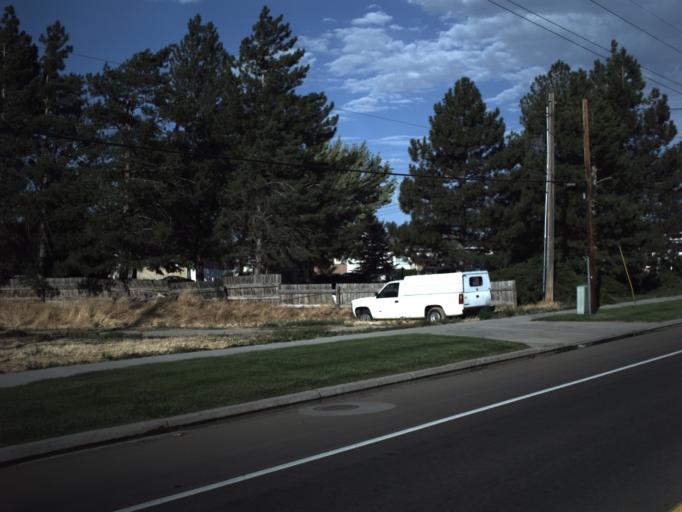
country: US
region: Utah
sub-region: Utah County
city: Spanish Fork
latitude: 40.0986
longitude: -111.6251
